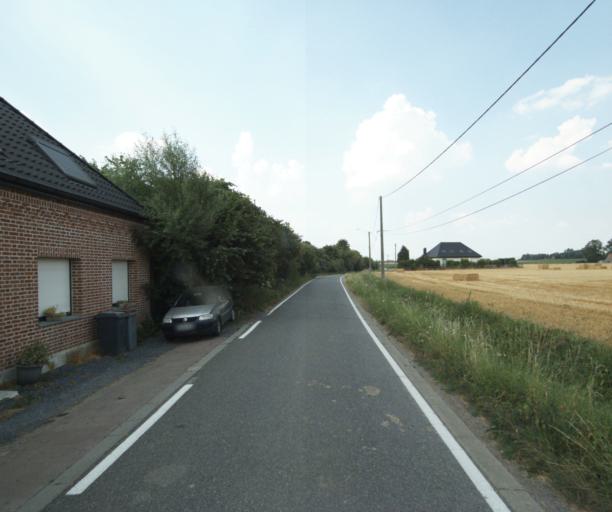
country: FR
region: Nord-Pas-de-Calais
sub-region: Departement du Nord
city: Linselles
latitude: 50.7262
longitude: 3.0596
